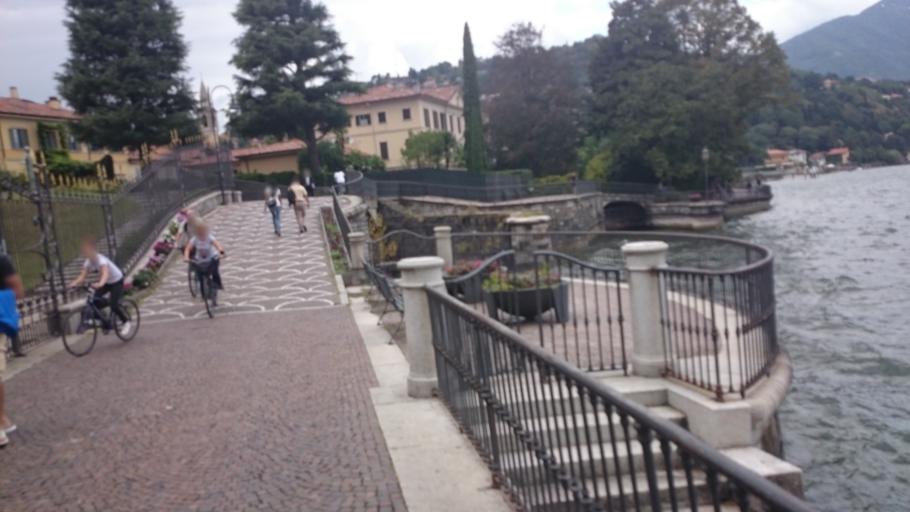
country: IT
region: Lombardy
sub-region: Provincia di Como
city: Como
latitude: 45.8154
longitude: 9.0677
